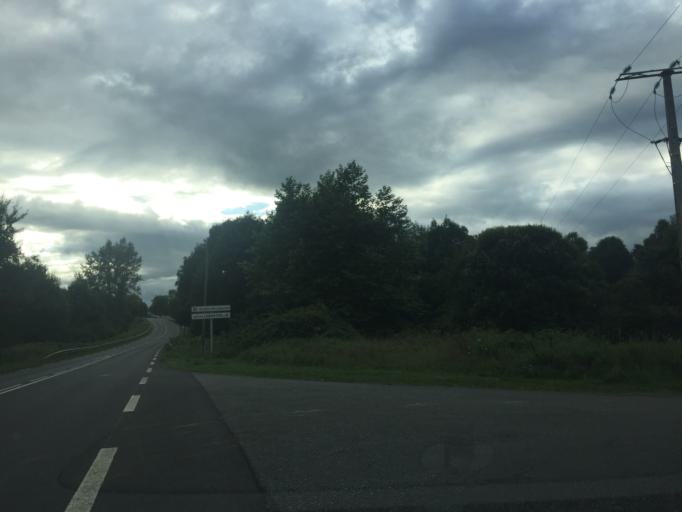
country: FR
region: Midi-Pyrenees
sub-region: Departement des Hautes-Pyrenees
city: Capvern
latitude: 43.1041
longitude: 0.3393
